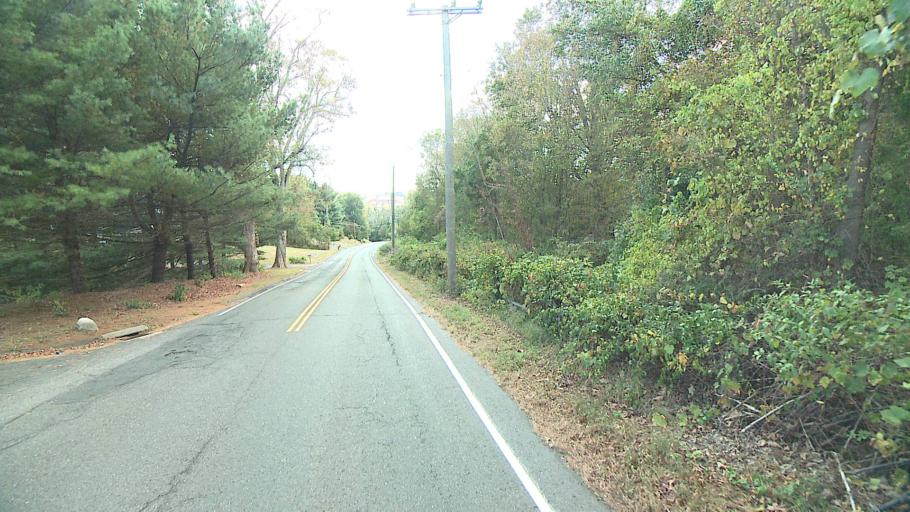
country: US
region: Connecticut
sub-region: New Haven County
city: Oxford
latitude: 41.4321
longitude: -73.0856
